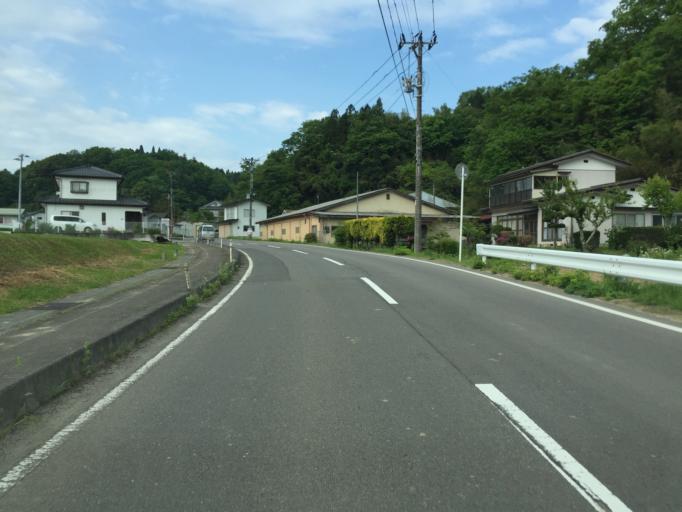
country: JP
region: Fukushima
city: Hobaramachi
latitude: 37.7189
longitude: 140.5921
